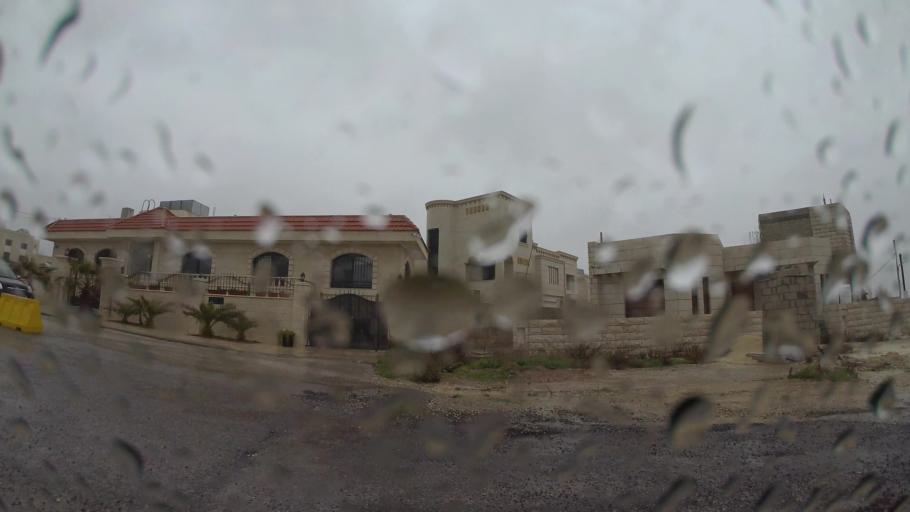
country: JO
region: Amman
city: Al Jubayhah
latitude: 32.0099
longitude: 35.9034
